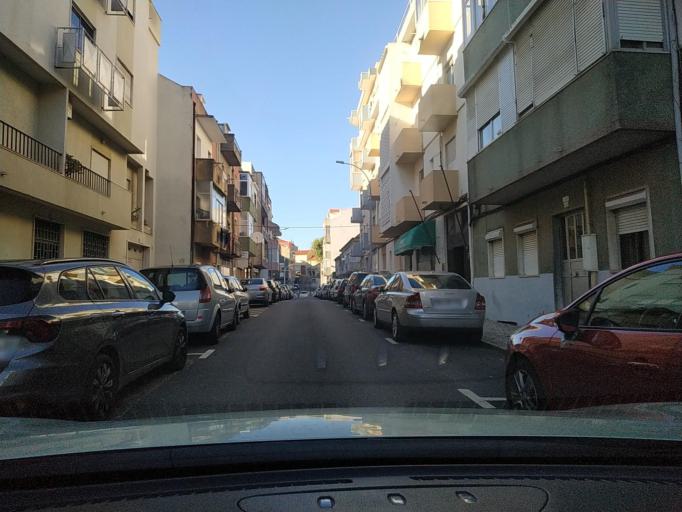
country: PT
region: Lisbon
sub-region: Odivelas
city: Pontinha
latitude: 38.7682
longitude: -9.2145
